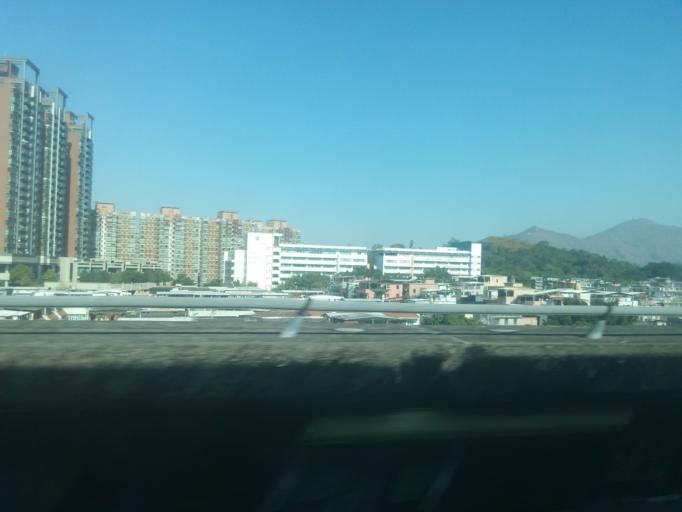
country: HK
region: Yuen Long
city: Yuen Long Kau Hui
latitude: 22.4471
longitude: 114.0308
